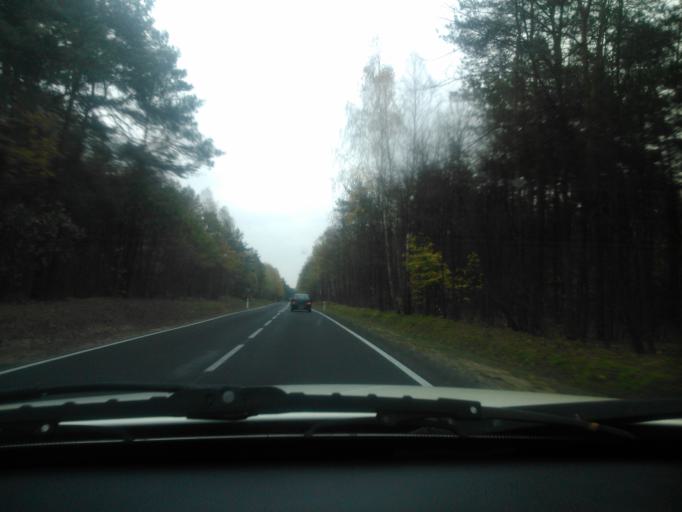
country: PL
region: Warmian-Masurian Voivodeship
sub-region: Powiat dzialdowski
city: Ilowo -Osada
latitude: 53.1196
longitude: 20.2904
